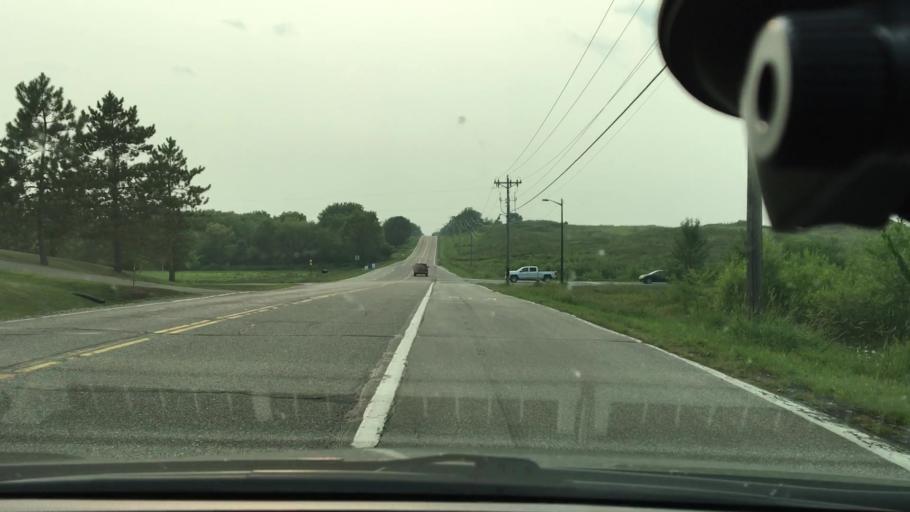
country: US
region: Minnesota
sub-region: Wright County
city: Otsego
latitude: 45.2525
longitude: -93.5631
